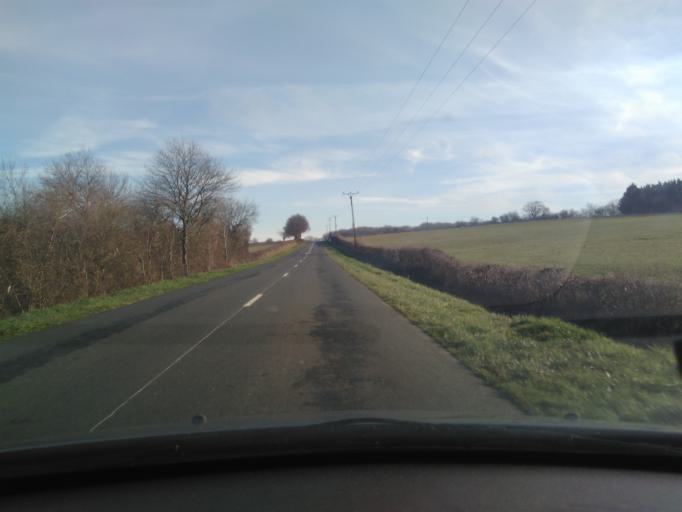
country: FR
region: Centre
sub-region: Departement de l'Indre
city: Montgivray
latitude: 46.6394
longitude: 2.0915
